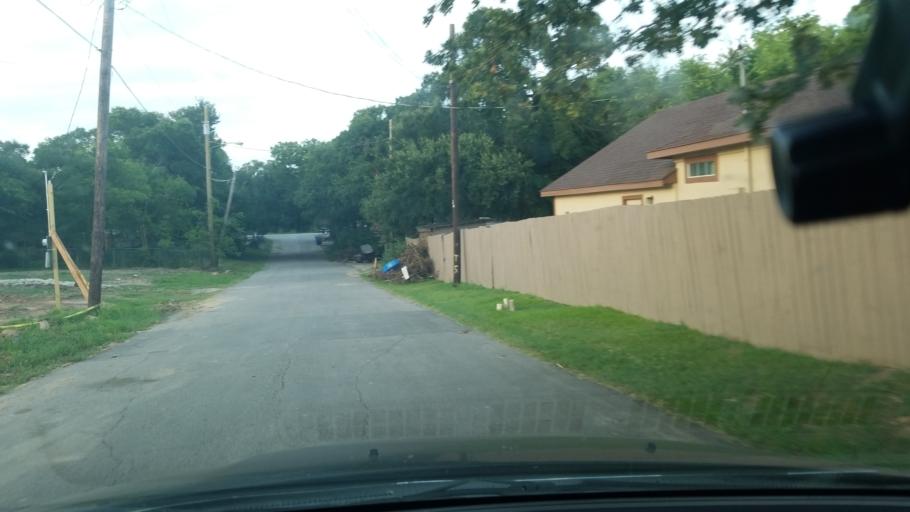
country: US
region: Texas
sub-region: Dallas County
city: Balch Springs
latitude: 32.7285
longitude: -96.6610
